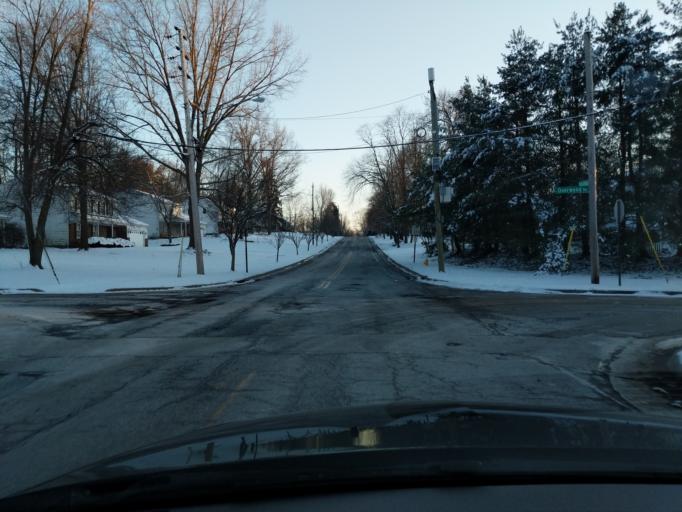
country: US
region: Ohio
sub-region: Summit County
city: Fairlawn
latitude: 41.1282
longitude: -81.5875
